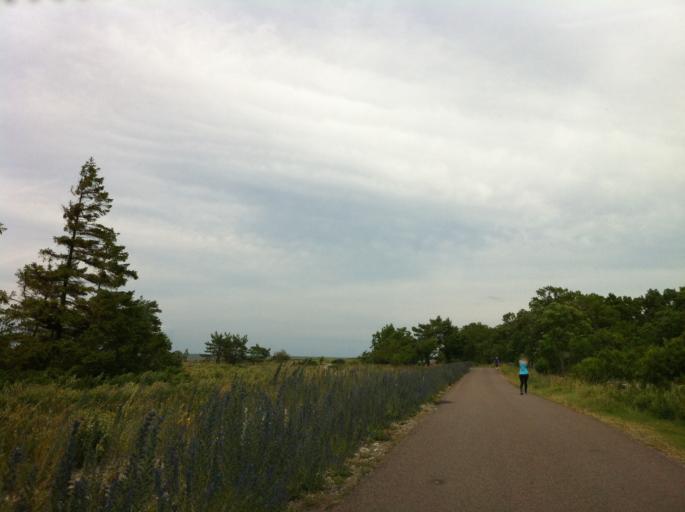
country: SE
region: Kalmar
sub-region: Oskarshamns Kommun
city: Oskarshamn
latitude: 57.3065
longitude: 16.9814
